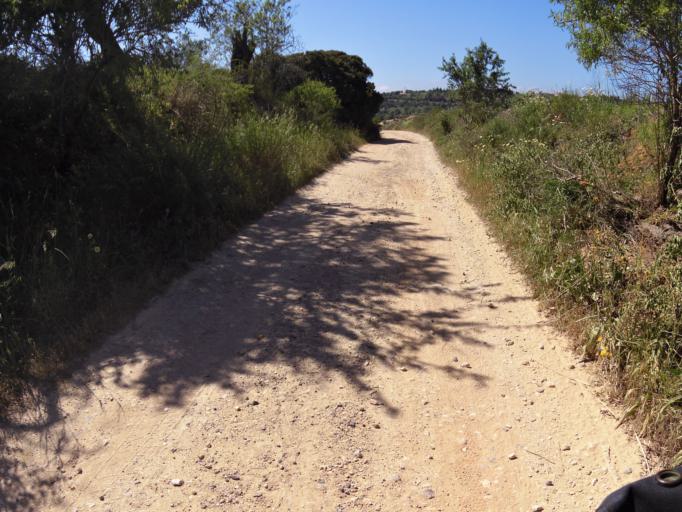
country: PT
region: Faro
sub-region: Lagos
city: Lagos
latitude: 37.0997
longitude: -8.7084
